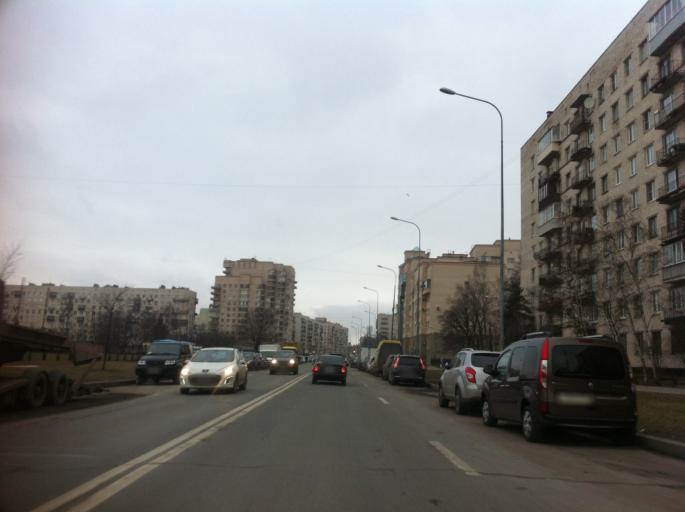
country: RU
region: St.-Petersburg
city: Dachnoye
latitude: 59.8384
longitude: 30.2414
